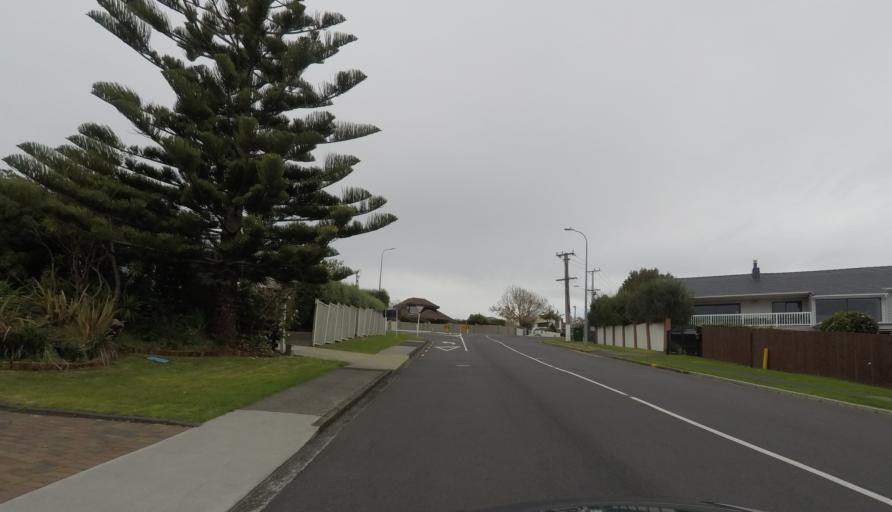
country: NZ
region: Auckland
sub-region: Auckland
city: Pakuranga
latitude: -36.8964
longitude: 174.9441
